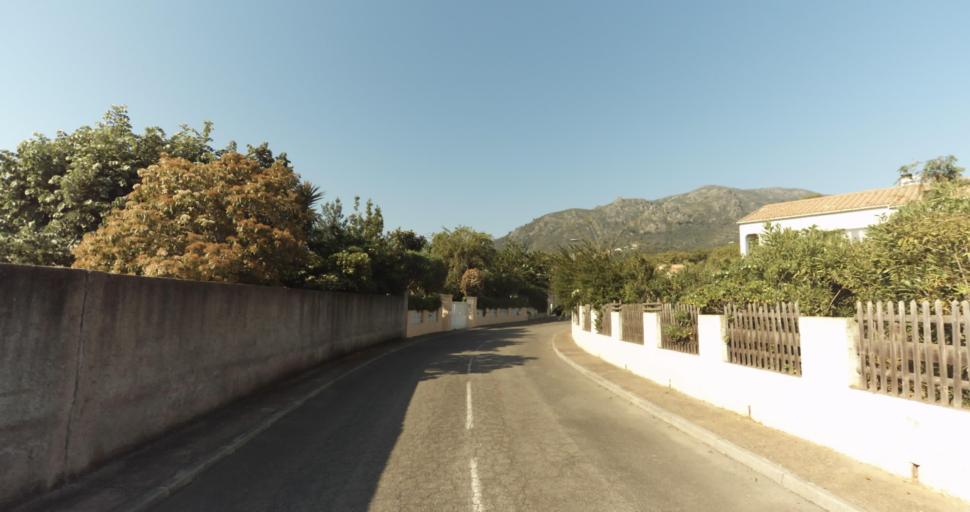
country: FR
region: Corsica
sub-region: Departement de la Haute-Corse
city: Biguglia
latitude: 42.6361
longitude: 9.4318
